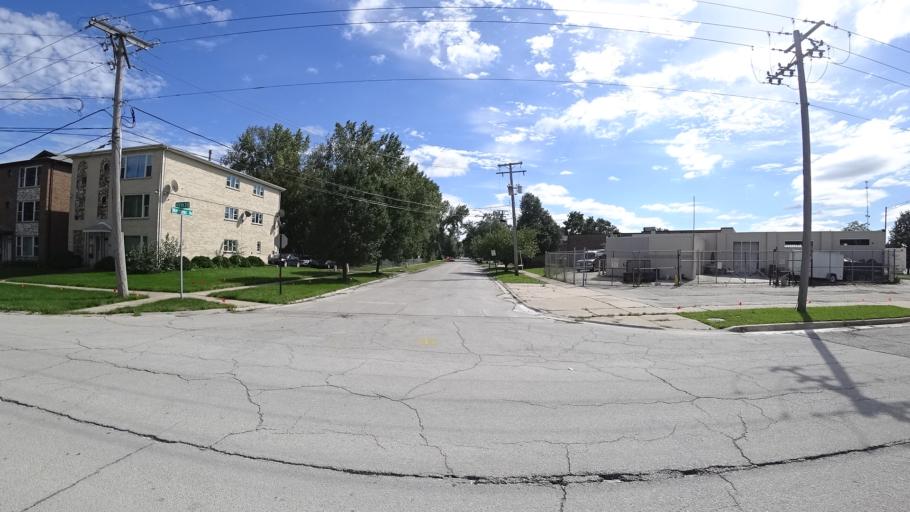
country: US
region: Illinois
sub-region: Cook County
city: Chicago Ridge
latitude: 41.7124
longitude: -87.7760
